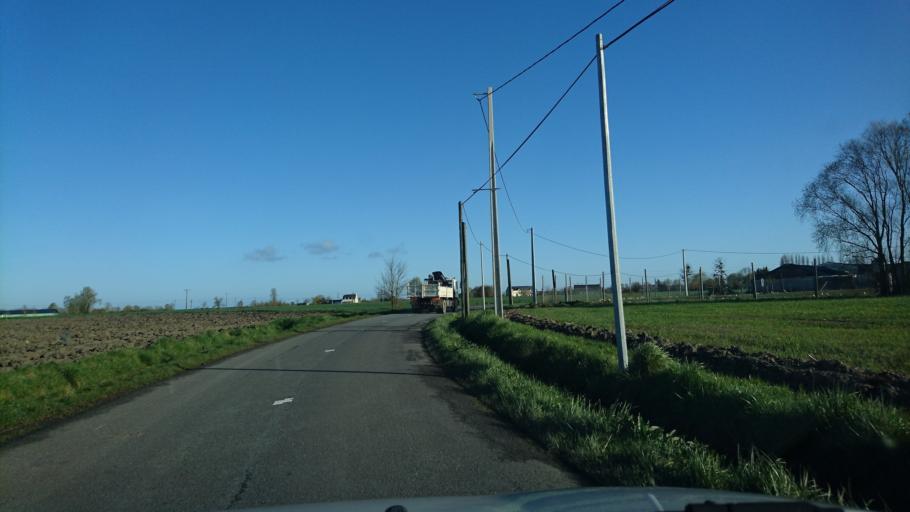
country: FR
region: Brittany
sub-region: Departement d'Ille-et-Vilaine
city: Cherrueix
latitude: 48.5937
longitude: -1.7185
